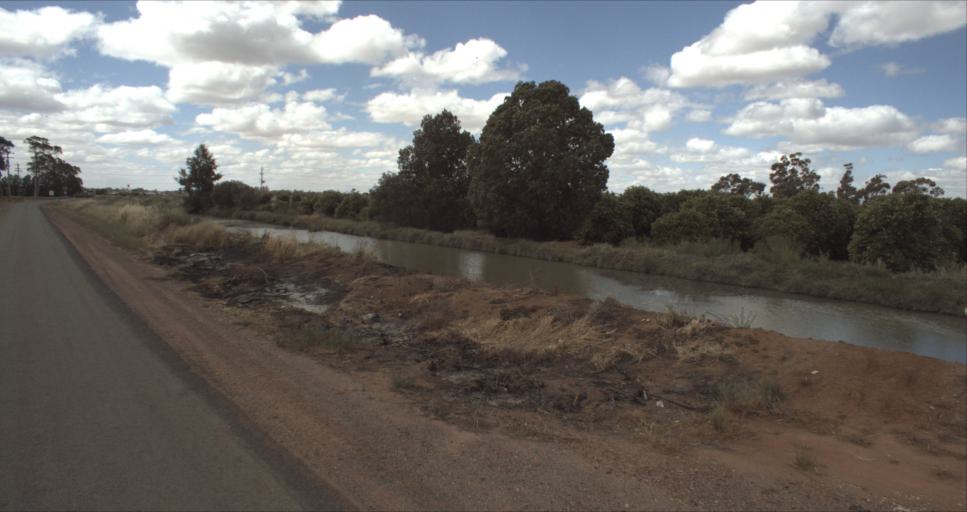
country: AU
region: New South Wales
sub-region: Leeton
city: Leeton
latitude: -34.5806
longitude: 146.3970
